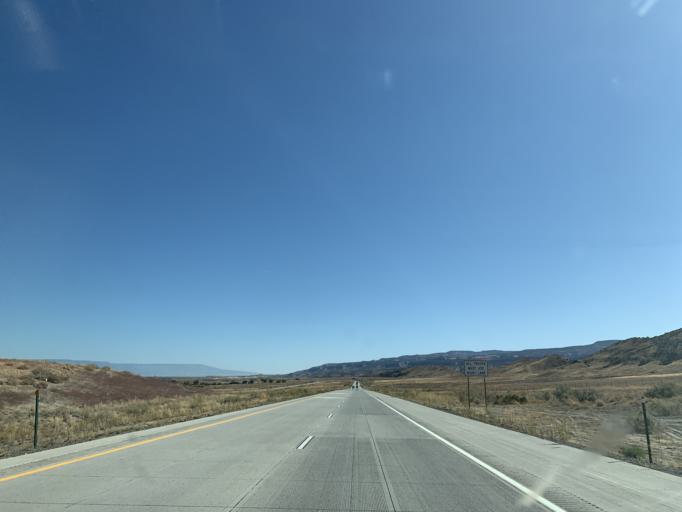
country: US
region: Colorado
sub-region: Mesa County
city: Loma
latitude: 39.1917
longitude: -108.8411
